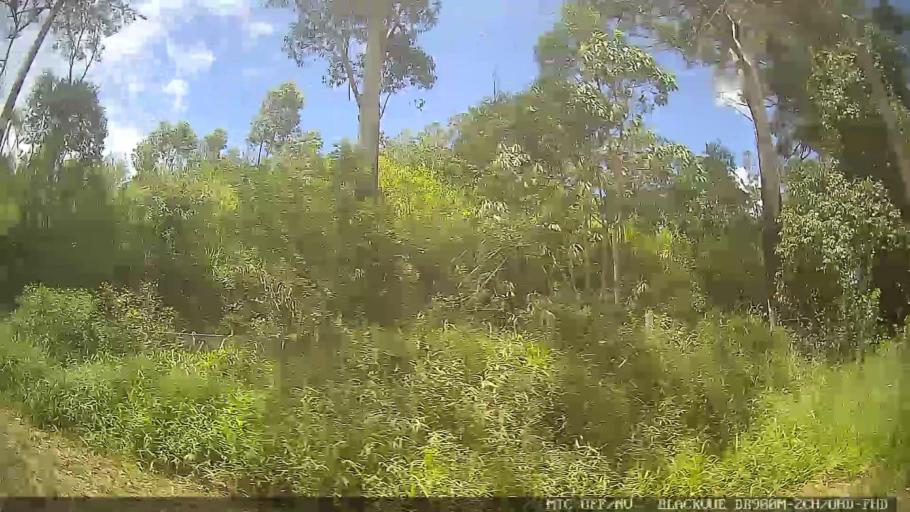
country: BR
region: Minas Gerais
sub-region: Extrema
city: Extrema
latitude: -22.7578
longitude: -46.4349
